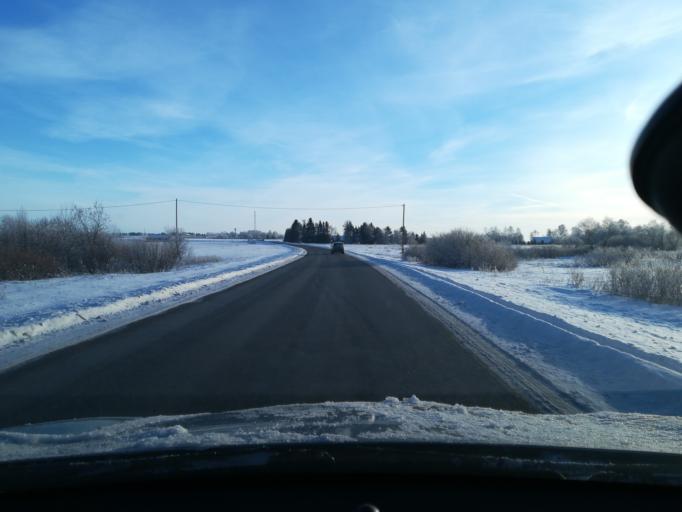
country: EE
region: Harju
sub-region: Harku vald
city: Tabasalu
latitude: 59.3705
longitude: 24.4756
